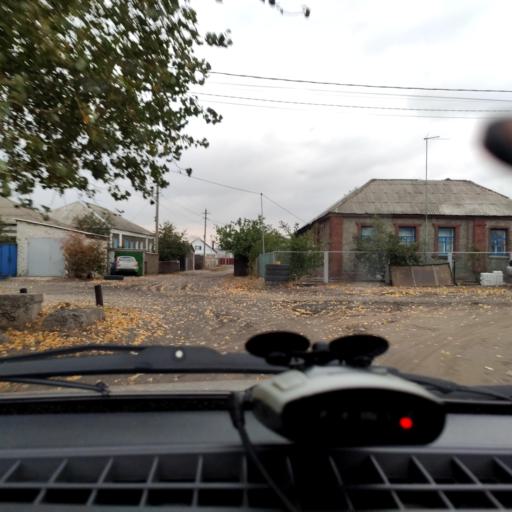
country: RU
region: Voronezj
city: Pridonskoy
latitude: 51.7040
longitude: 39.0692
